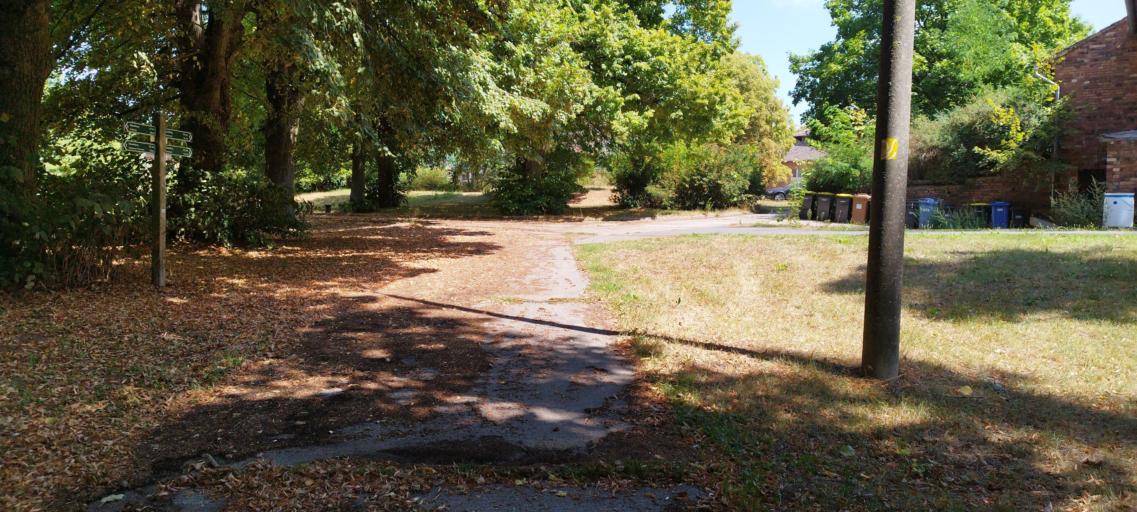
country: DE
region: Brandenburg
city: Wiesenburg
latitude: 52.1389
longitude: 12.4799
